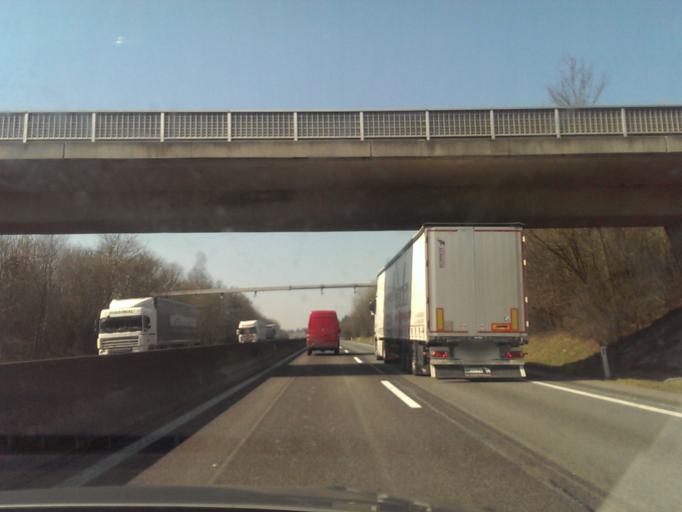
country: AT
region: Upper Austria
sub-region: Politischer Bezirk Ried im Innkreis
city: Ried im Innkreis
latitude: 48.2355
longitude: 13.5824
